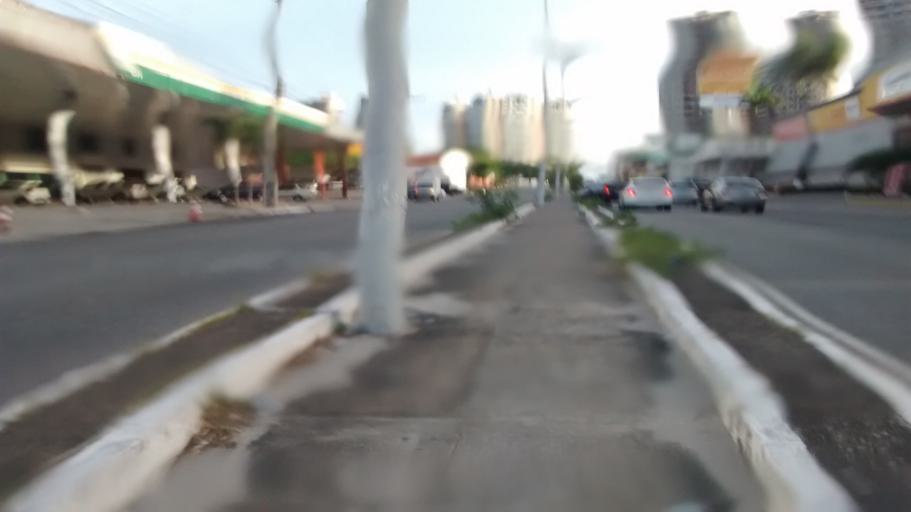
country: BR
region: Ceara
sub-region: Fortaleza
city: Fortaleza
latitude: -3.7614
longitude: -38.4932
